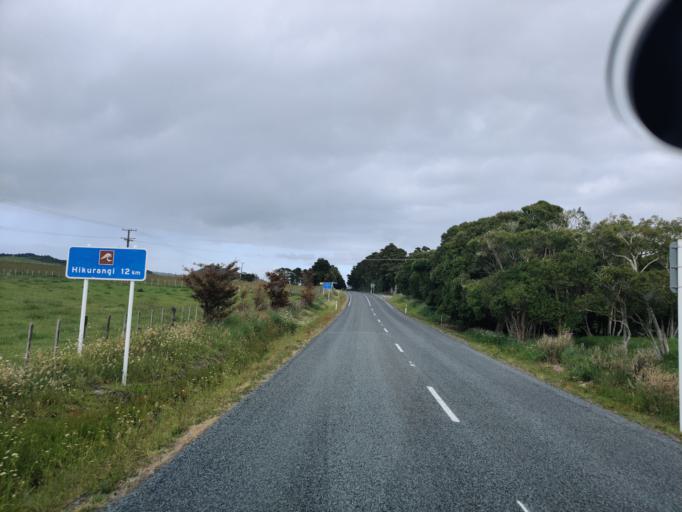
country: NZ
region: Northland
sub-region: Whangarei
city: Ngunguru
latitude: -35.5631
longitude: 174.3899
